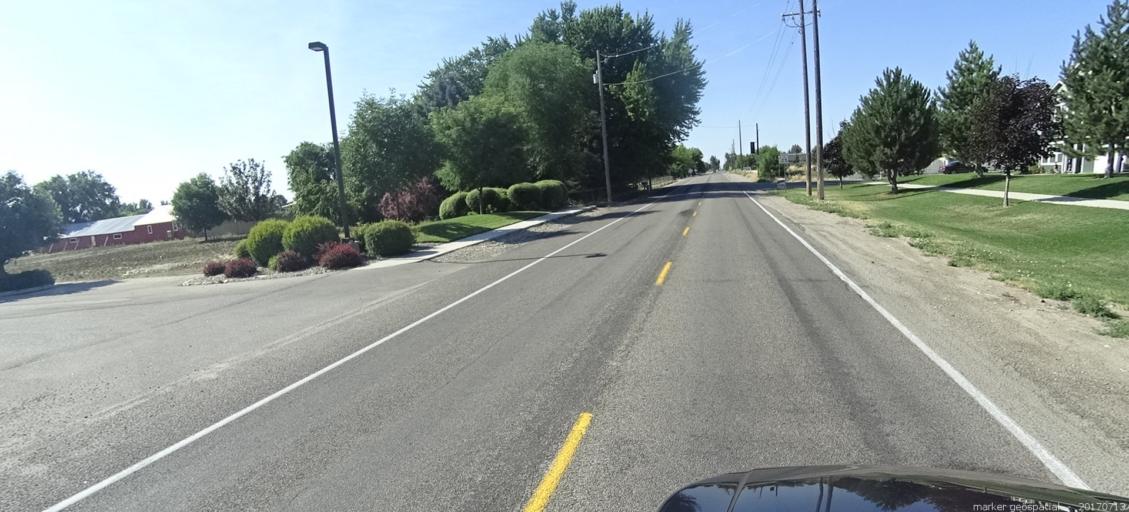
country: US
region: Idaho
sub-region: Ada County
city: Kuna
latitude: 43.5000
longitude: -116.4137
